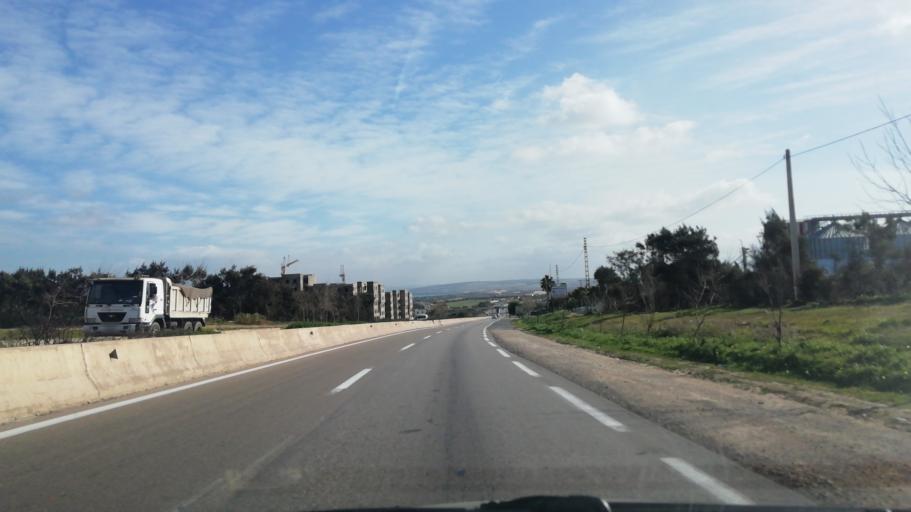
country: DZ
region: Oran
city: Ain el Bya
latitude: 35.7863
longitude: -0.1754
